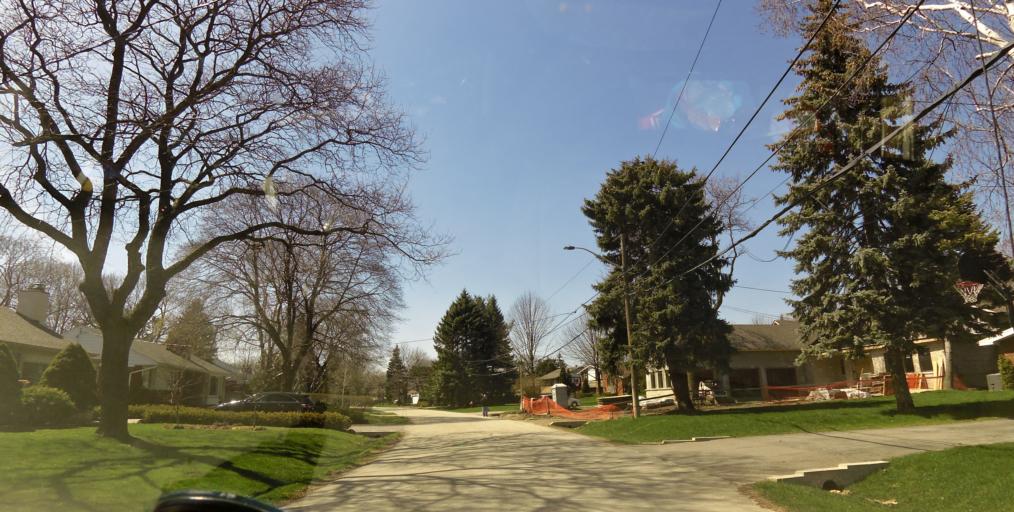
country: CA
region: Ontario
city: Etobicoke
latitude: 43.6028
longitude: -79.5586
